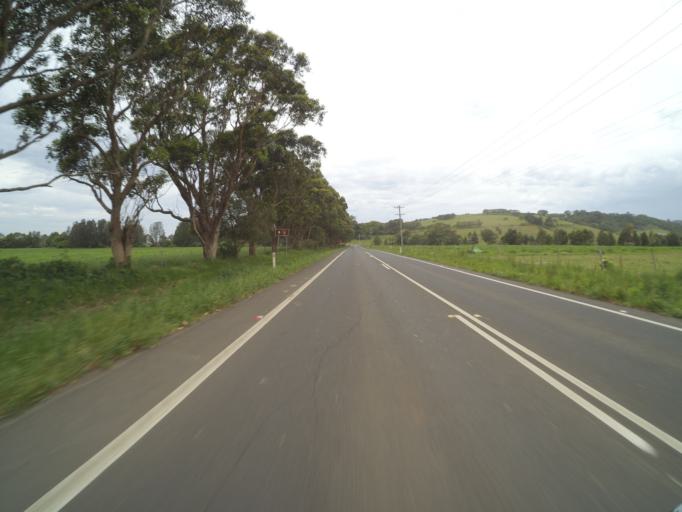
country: AU
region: New South Wales
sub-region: Kiama
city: Jamberoo
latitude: -34.6514
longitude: 150.7946
